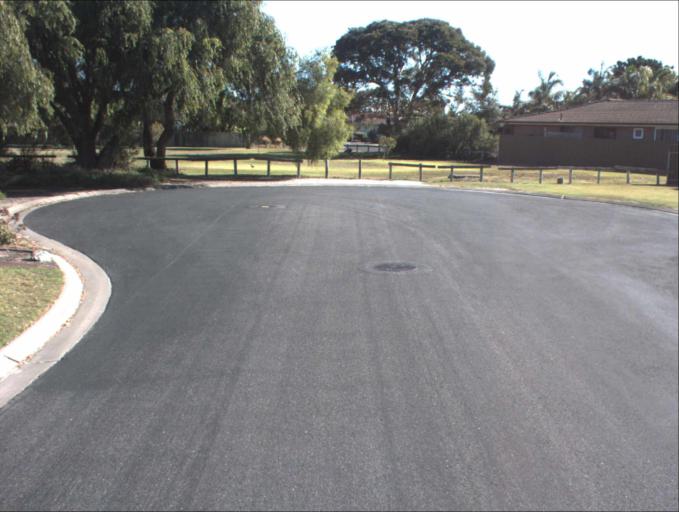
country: AU
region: South Australia
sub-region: Port Adelaide Enfield
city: Birkenhead
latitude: -34.7827
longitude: 138.4983
